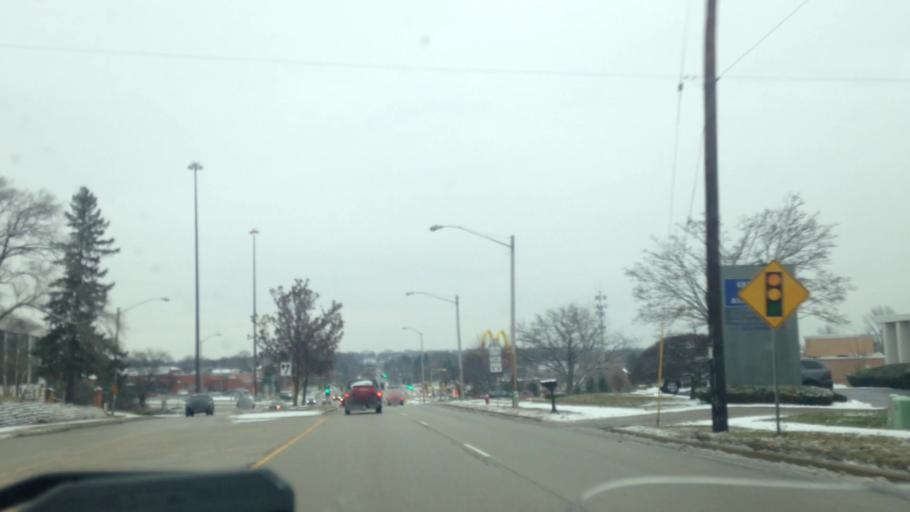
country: US
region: Wisconsin
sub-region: Waukesha County
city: Menomonee Falls
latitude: 43.1677
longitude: -88.1039
